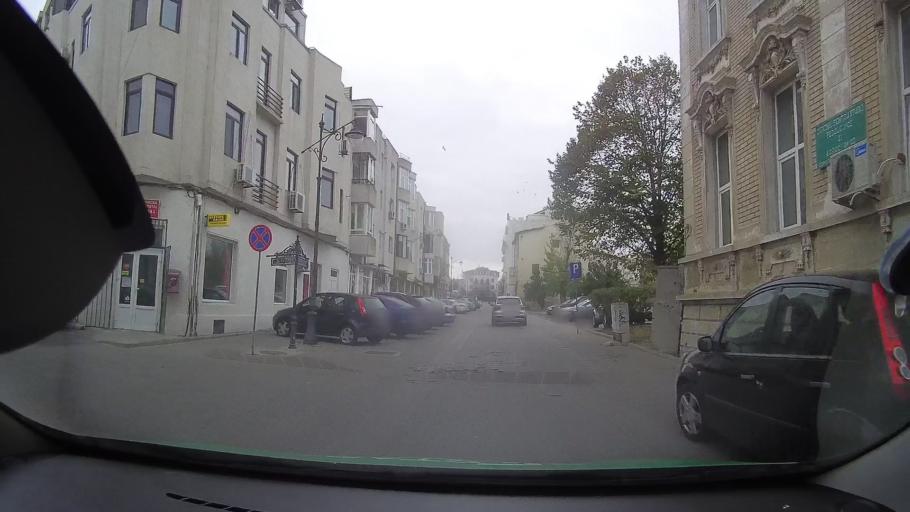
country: RO
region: Constanta
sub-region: Municipiul Constanta
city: Constanta
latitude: 44.1732
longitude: 28.6608
